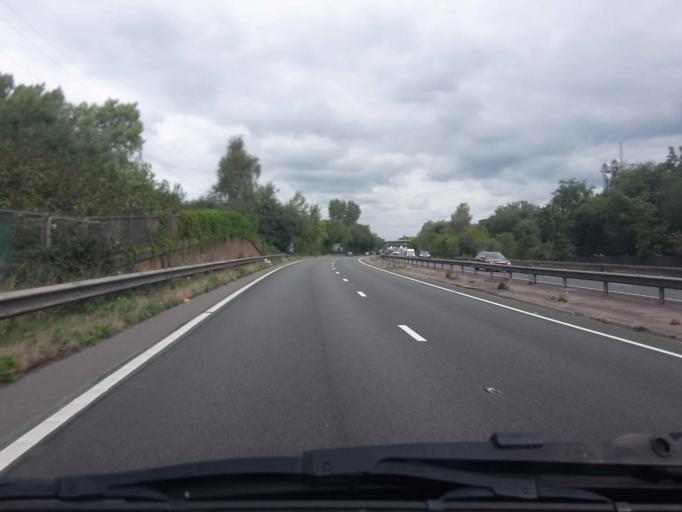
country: GB
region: England
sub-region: Hampshire
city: Aldershot
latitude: 51.2632
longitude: -0.7356
